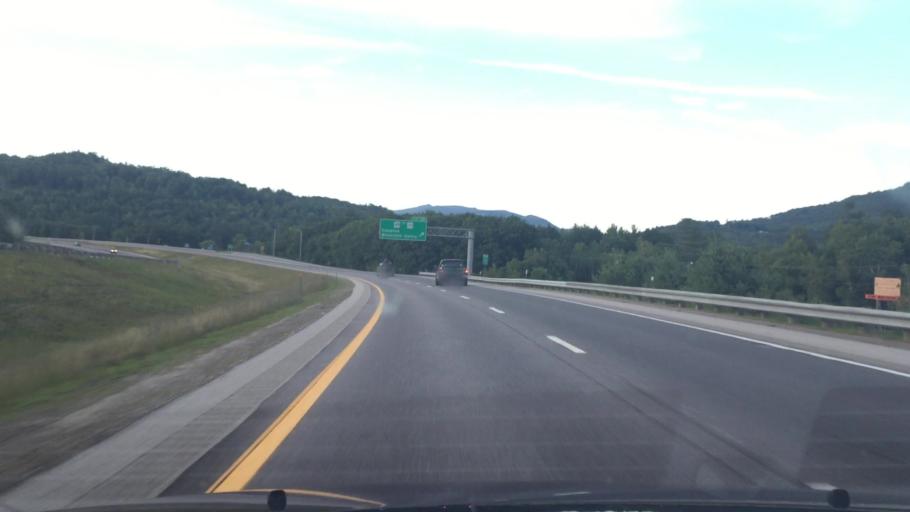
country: US
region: New Hampshire
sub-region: Grafton County
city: Thornton
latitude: 43.8445
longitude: -71.6464
